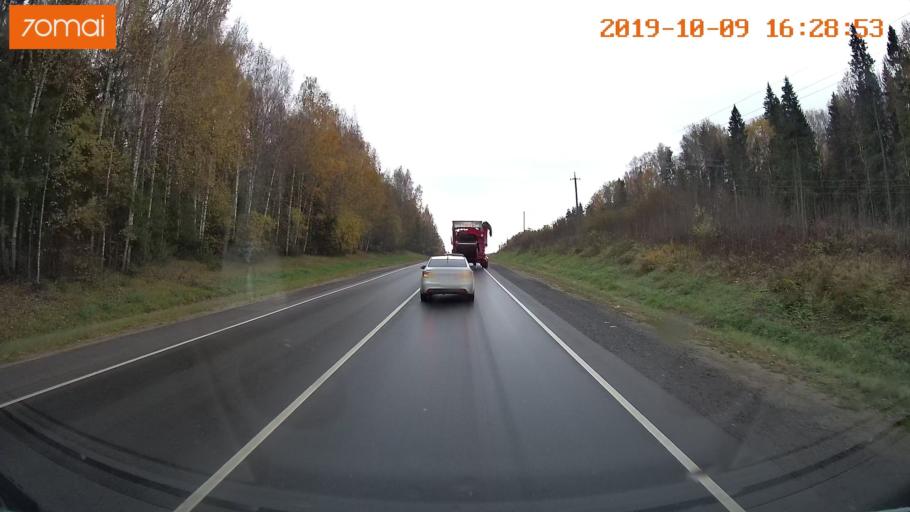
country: RU
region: Kostroma
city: Oktyabr'skiy
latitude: 57.6266
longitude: 40.9339
